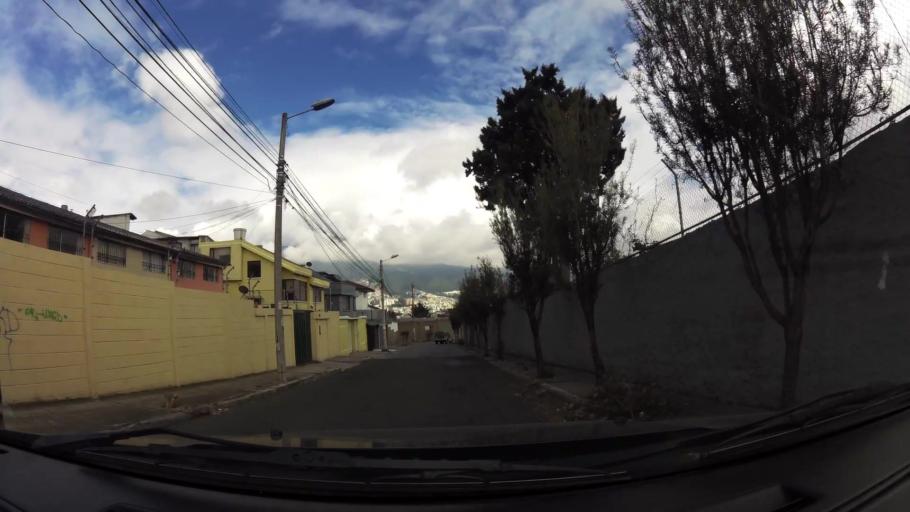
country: EC
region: Pichincha
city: Quito
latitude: -0.1592
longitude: -78.4700
